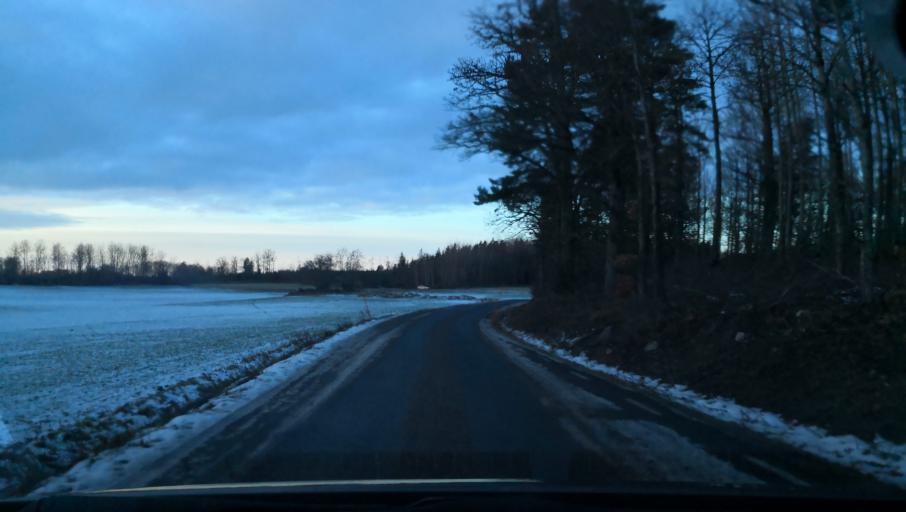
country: SE
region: Soedermanland
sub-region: Eskilstuna Kommun
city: Skogstorp
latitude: 59.2319
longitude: 16.3341
